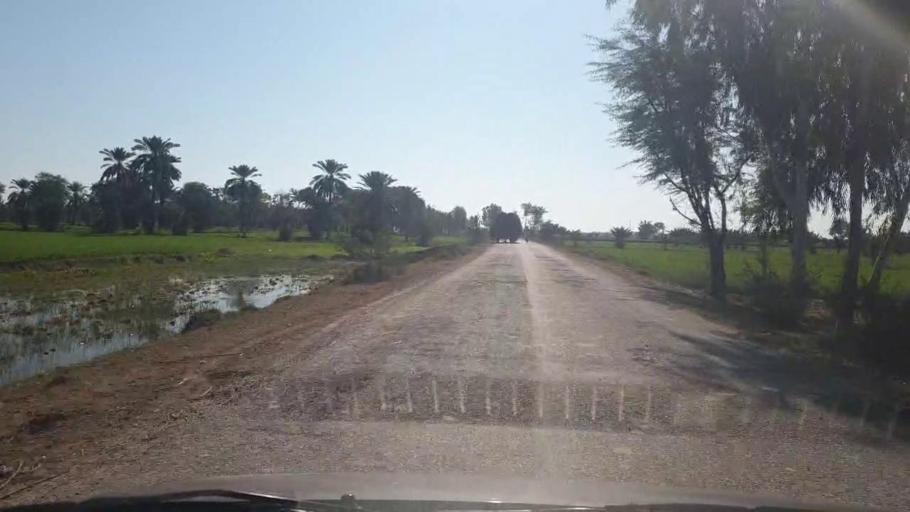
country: PK
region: Sindh
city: Bozdar
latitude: 27.1670
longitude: 68.6433
